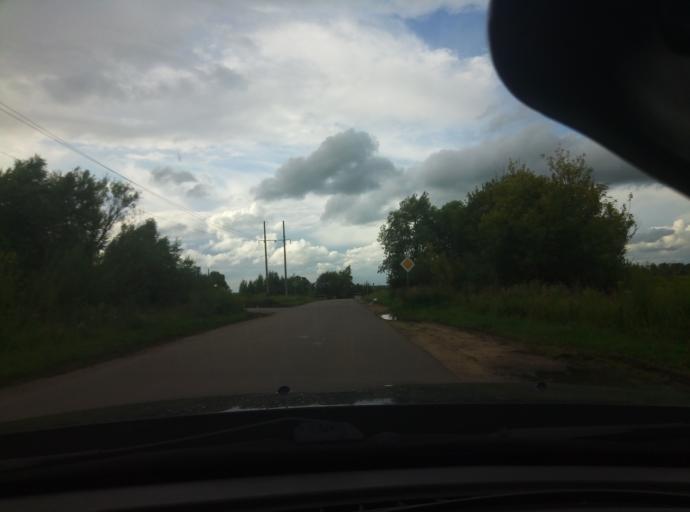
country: RU
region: Tula
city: Bolokhovo
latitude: 54.0851
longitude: 37.8376
